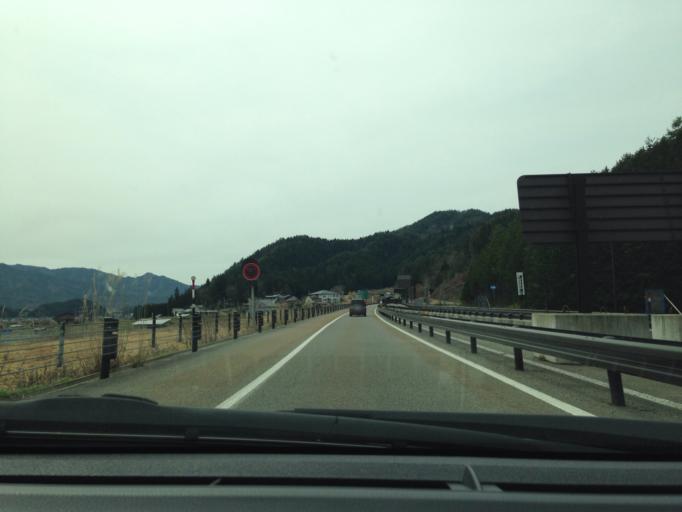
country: JP
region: Gifu
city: Takayama
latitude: 36.1645
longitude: 137.2272
